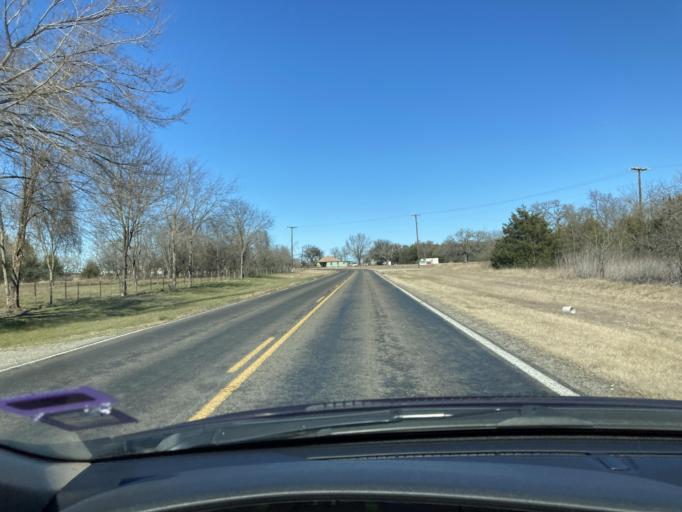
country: US
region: Texas
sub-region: Navarro County
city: Corsicana
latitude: 32.0598
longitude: -96.4988
